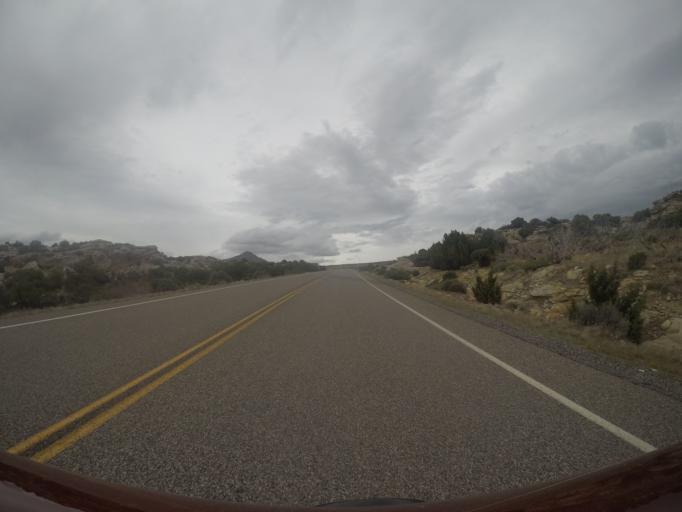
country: US
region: Wyoming
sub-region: Big Horn County
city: Lovell
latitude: 44.9942
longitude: -108.2611
